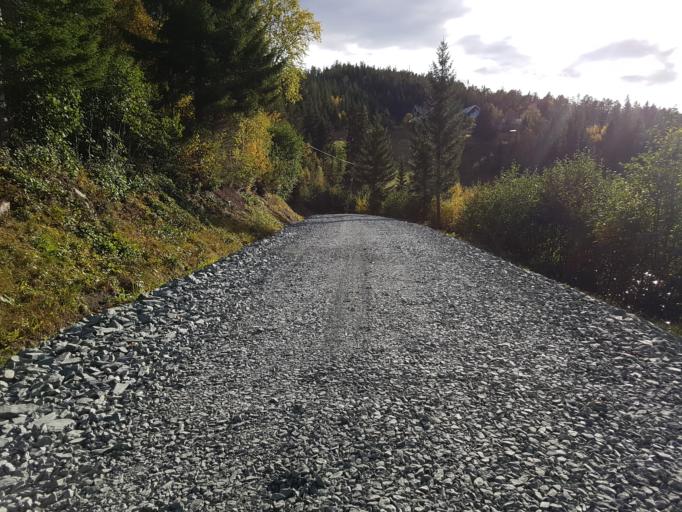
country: NO
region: Sor-Trondelag
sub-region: Klaebu
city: Klaebu
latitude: 63.3423
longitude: 10.5845
